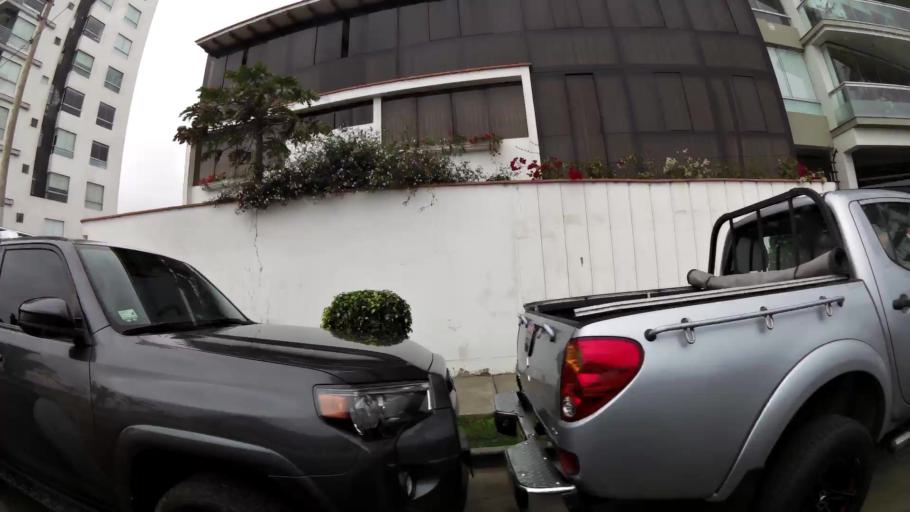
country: PE
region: Lima
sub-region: Lima
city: Surco
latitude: -12.1589
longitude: -77.0241
